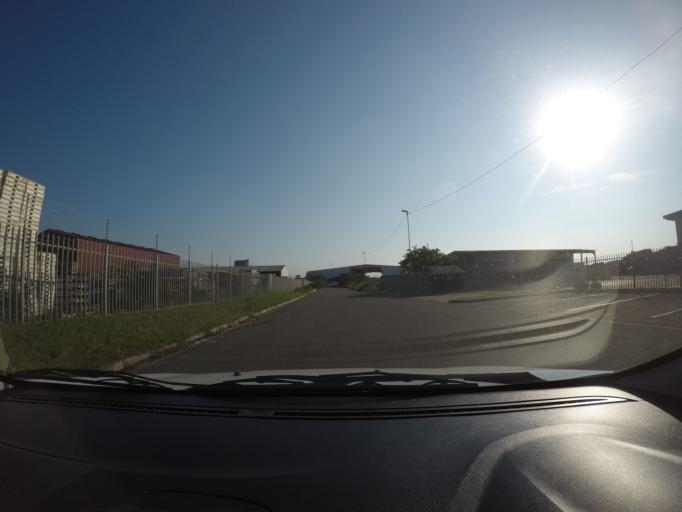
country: ZA
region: KwaZulu-Natal
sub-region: uThungulu District Municipality
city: Richards Bay
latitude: -28.7508
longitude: 32.0155
